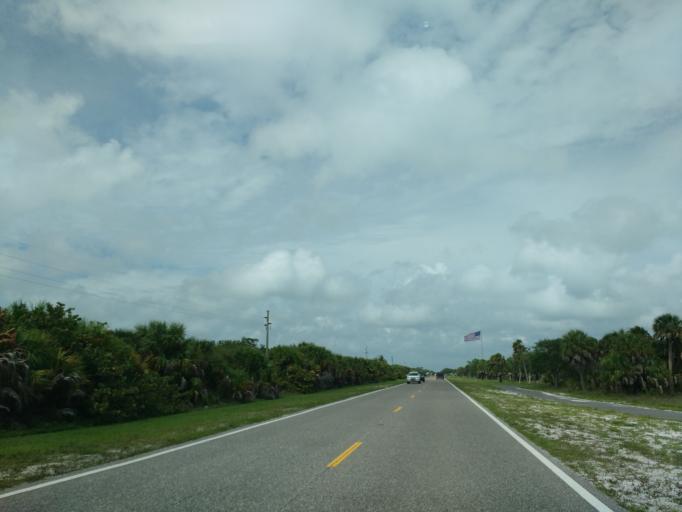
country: US
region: Florida
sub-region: Pinellas County
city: Tierra Verde
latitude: 27.6213
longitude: -82.7195
